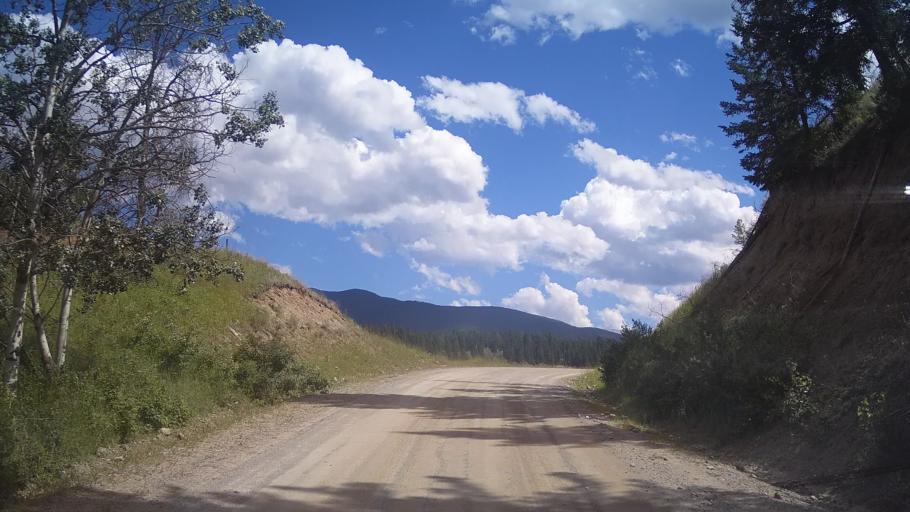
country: CA
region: British Columbia
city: Lillooet
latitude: 51.3028
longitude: -121.9849
